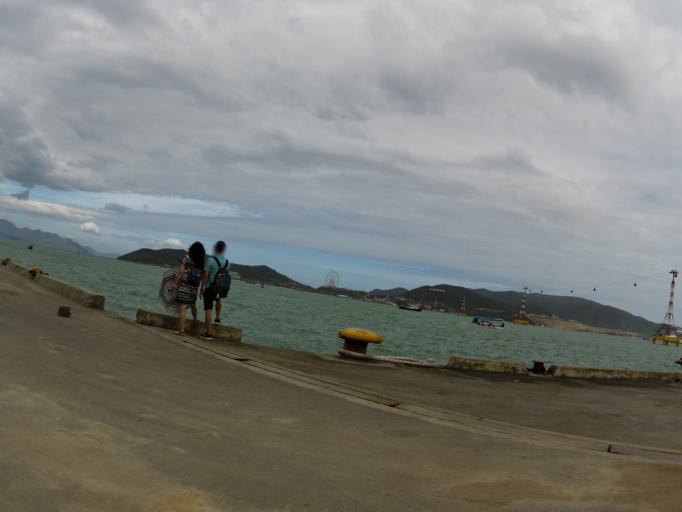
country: VN
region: Khanh Hoa
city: Nha Trang
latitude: 12.2056
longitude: 109.2166
